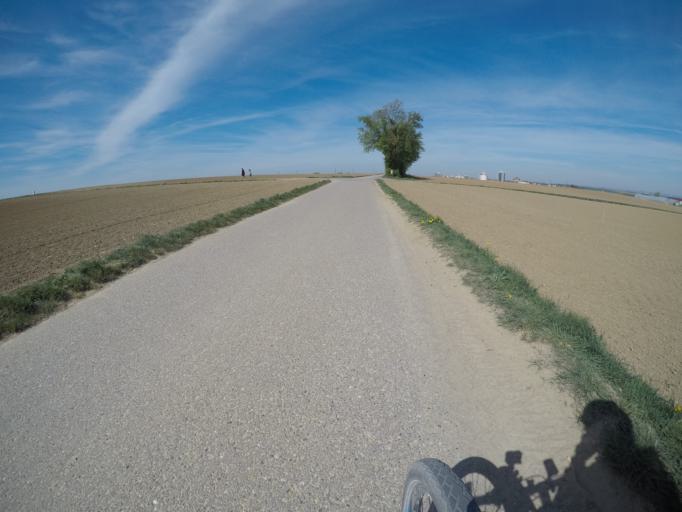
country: DE
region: Baden-Wuerttemberg
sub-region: Regierungsbezirk Stuttgart
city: Ditzingen
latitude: 48.8280
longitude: 9.0381
